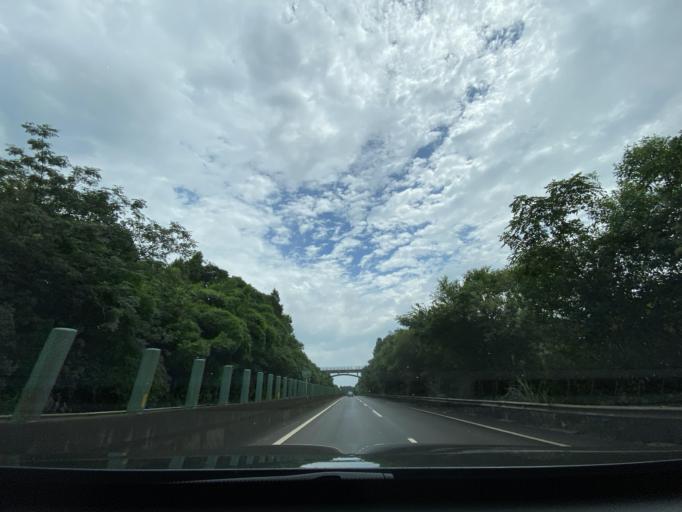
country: CN
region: Sichuan
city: Jiancheng
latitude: 30.3051
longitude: 104.5784
